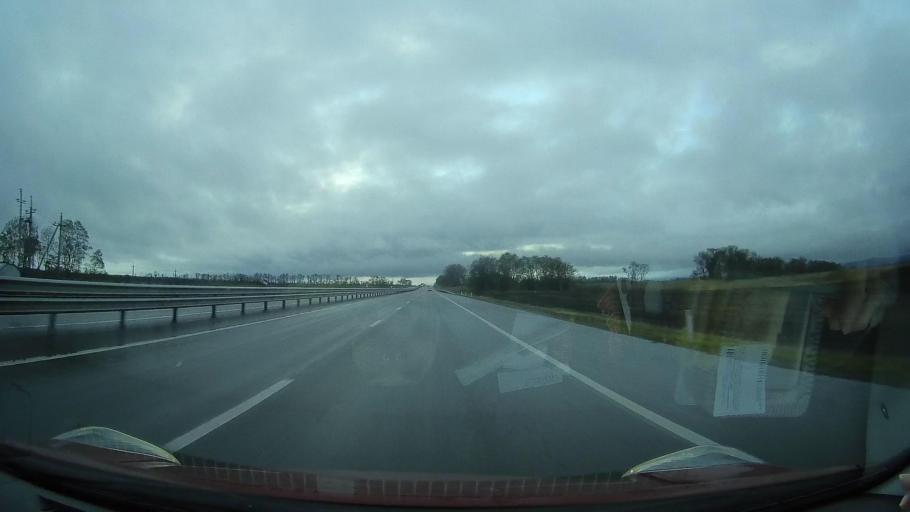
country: RU
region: Stavropol'skiy
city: Zavetnoye
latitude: 44.7856
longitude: 41.5173
